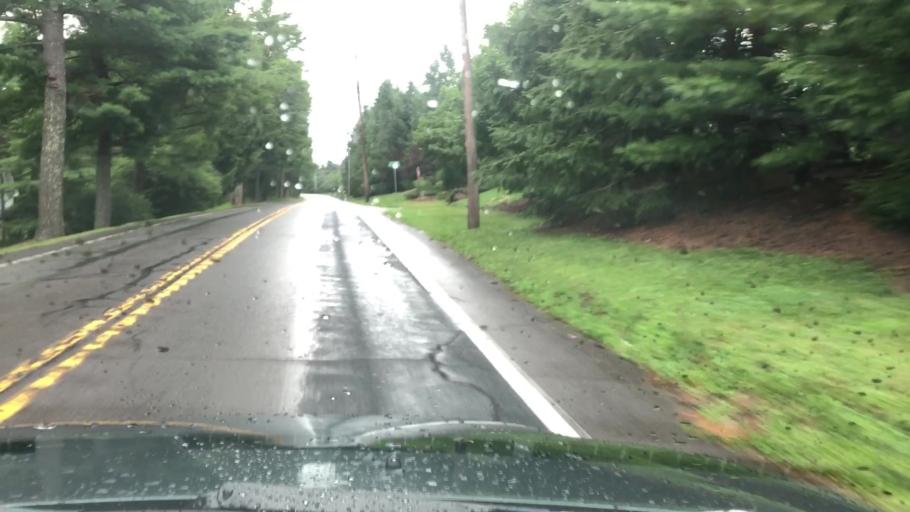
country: US
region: Pennsylvania
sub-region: Monroe County
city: Mountainhome
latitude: 41.2155
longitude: -75.2363
